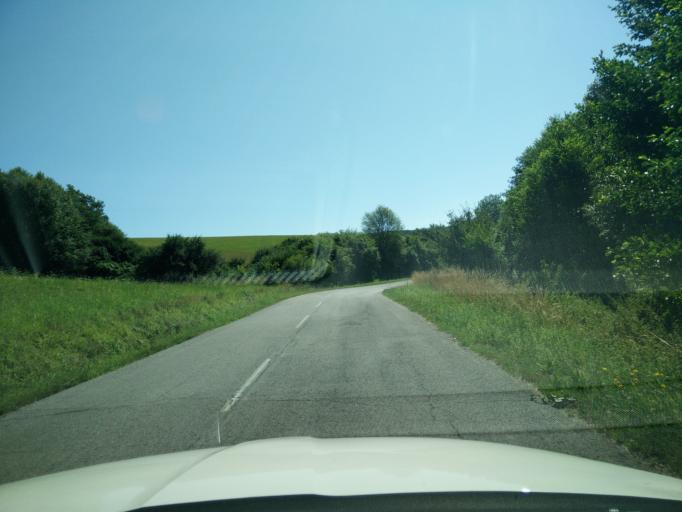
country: SK
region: Nitriansky
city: Prievidza
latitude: 48.7860
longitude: 18.7001
